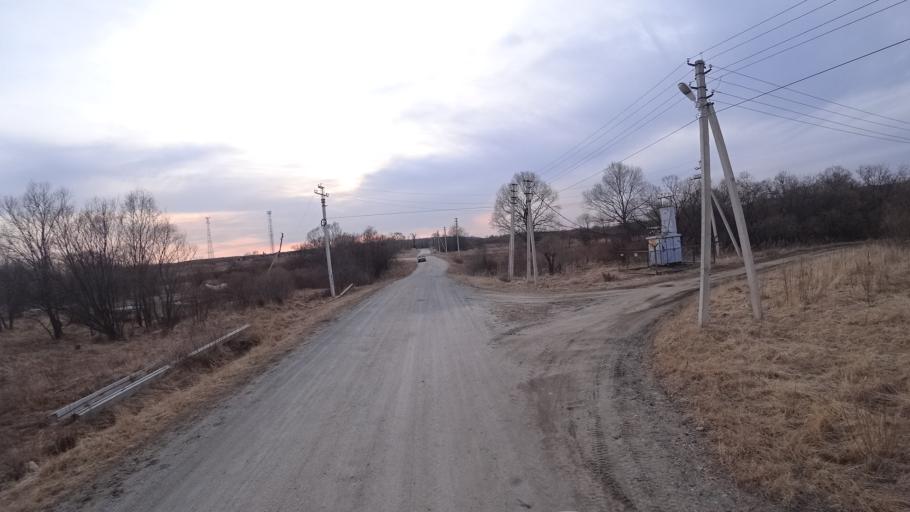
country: RU
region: Amur
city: Bureya
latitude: 50.0206
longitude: 129.7661
